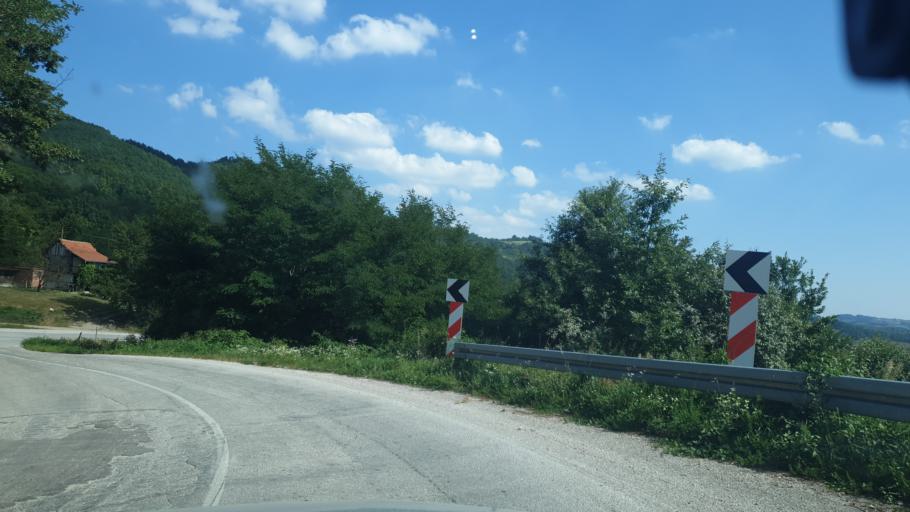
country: RS
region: Central Serbia
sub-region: Zlatiborski Okrug
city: Kosjeric
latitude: 43.9936
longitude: 20.0477
